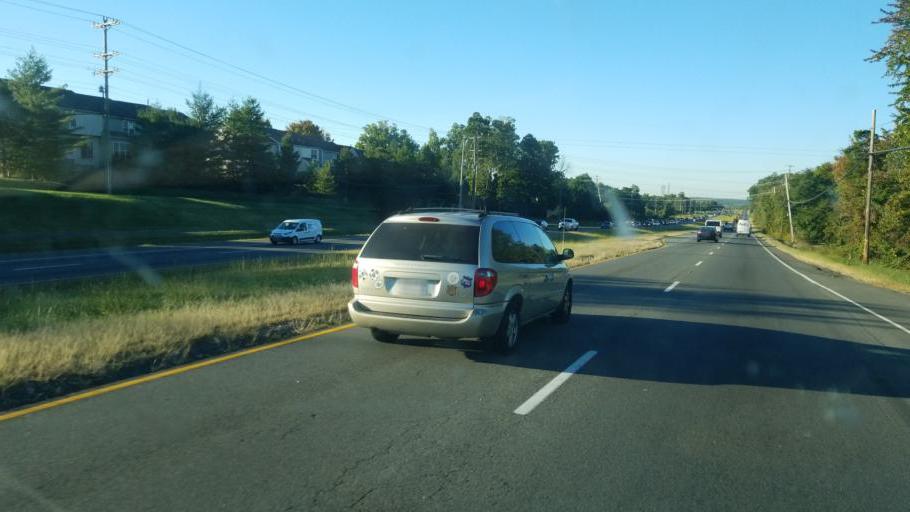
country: US
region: Virginia
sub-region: Fairfax County
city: Centreville
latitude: 38.8256
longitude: -77.4382
